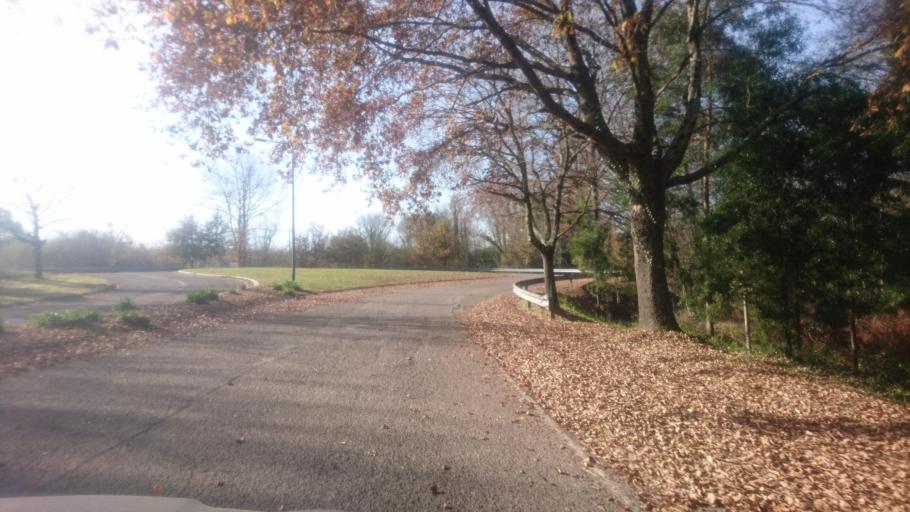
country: PT
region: Aveiro
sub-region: Santa Maria da Feira
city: Rio Meao
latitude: 40.9313
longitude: -8.5770
